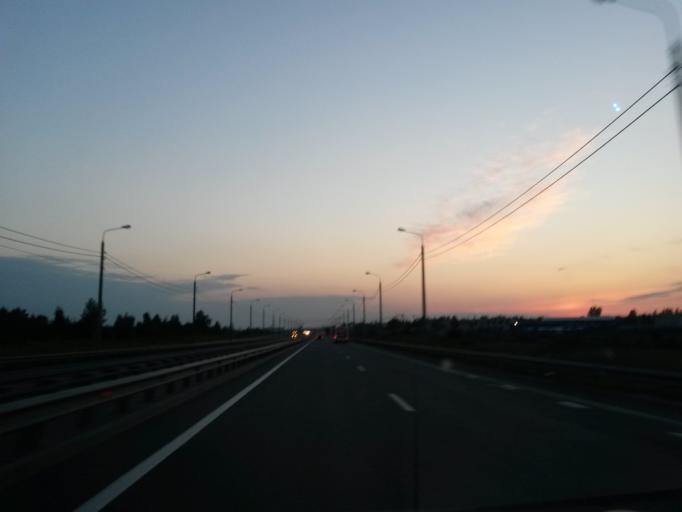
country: RU
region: Jaroslavl
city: Yaroslavl
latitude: 57.6685
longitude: 39.8075
